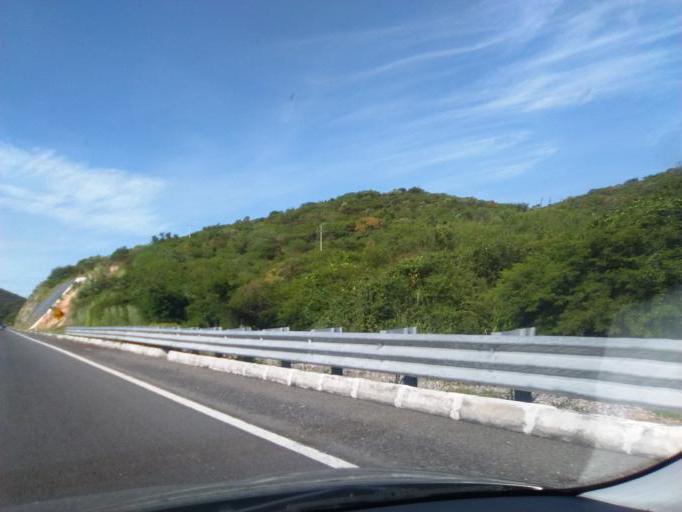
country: MX
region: Guerrero
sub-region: Huitzuco de los Figueroa
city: Ciudad de Huitzuco
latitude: 18.1494
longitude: -99.2123
